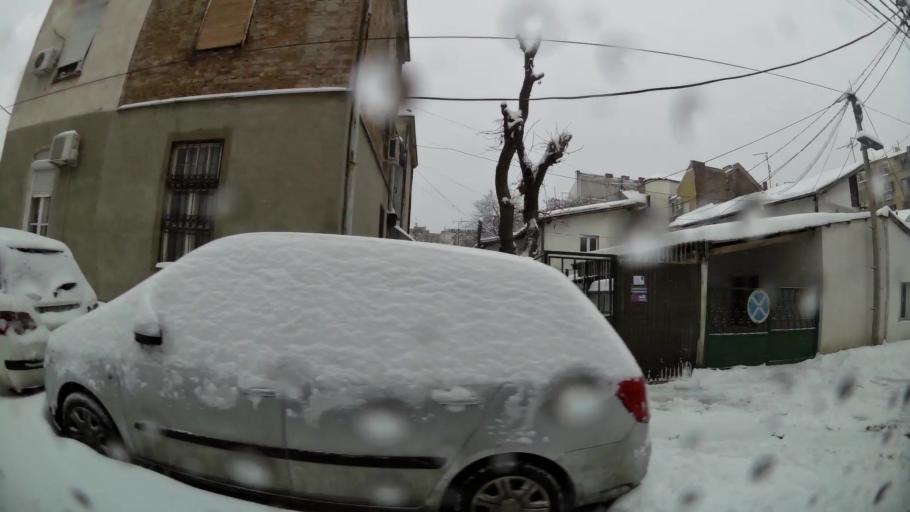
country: RS
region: Central Serbia
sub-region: Belgrade
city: Stari Grad
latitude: 44.8227
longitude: 20.4669
